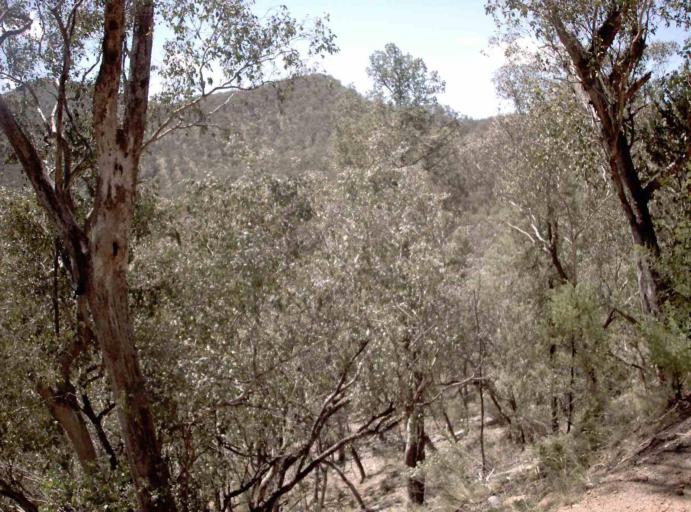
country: AU
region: New South Wales
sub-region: Snowy River
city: Jindabyne
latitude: -37.0565
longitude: 148.5336
